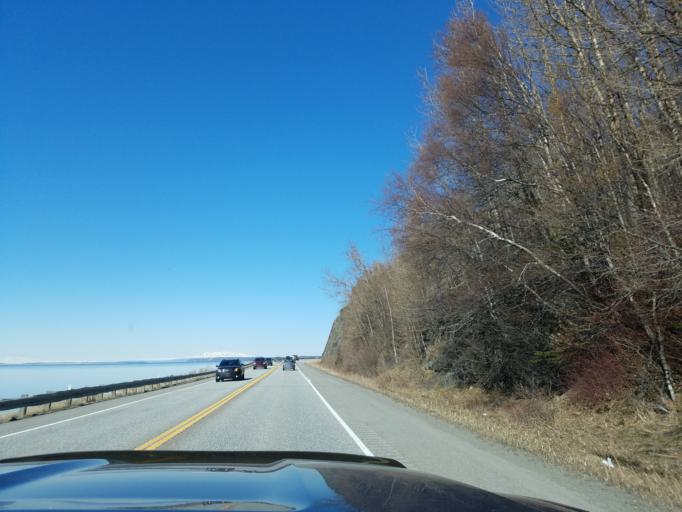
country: US
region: Alaska
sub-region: Anchorage Municipality
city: Anchorage
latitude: 61.0372
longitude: -149.7804
